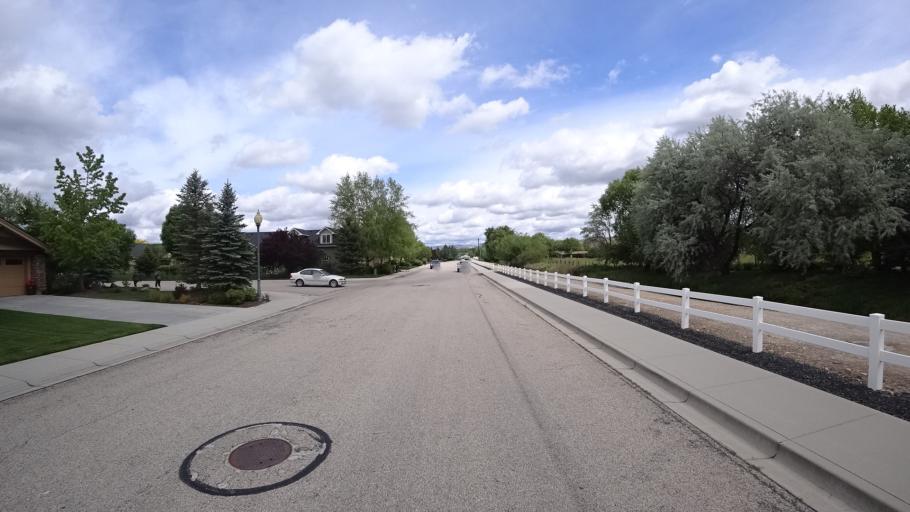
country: US
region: Idaho
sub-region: Ada County
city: Eagle
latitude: 43.6751
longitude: -116.3043
